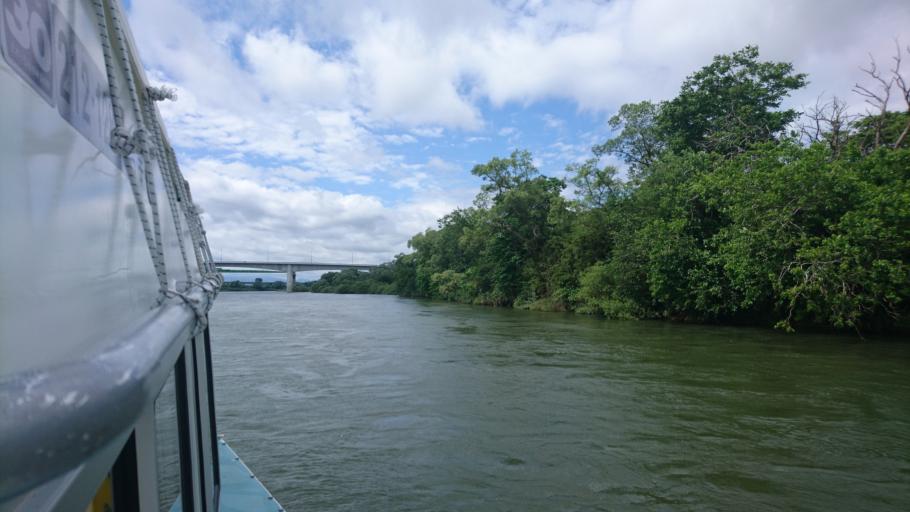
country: JP
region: Iwate
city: Ichinoseki
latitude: 38.9515
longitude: 141.1633
